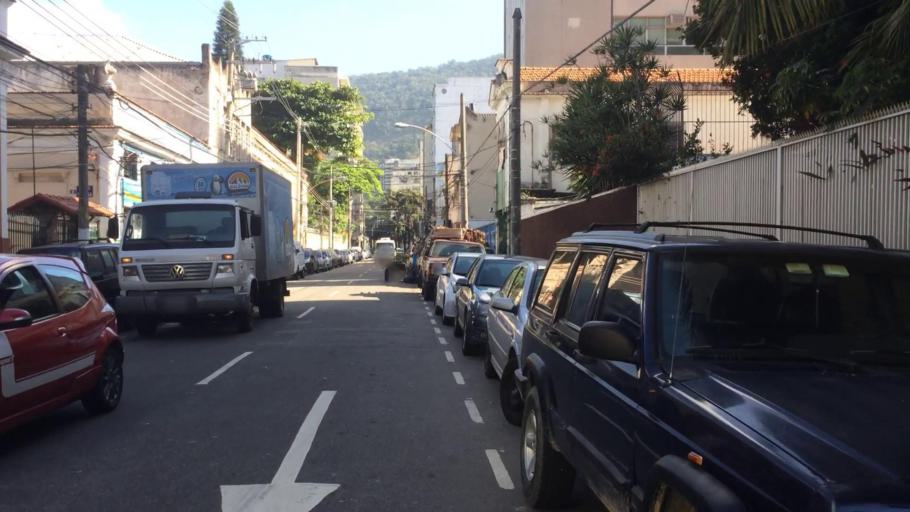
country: BR
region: Rio de Janeiro
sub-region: Rio De Janeiro
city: Rio de Janeiro
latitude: -22.9351
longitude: -43.1816
